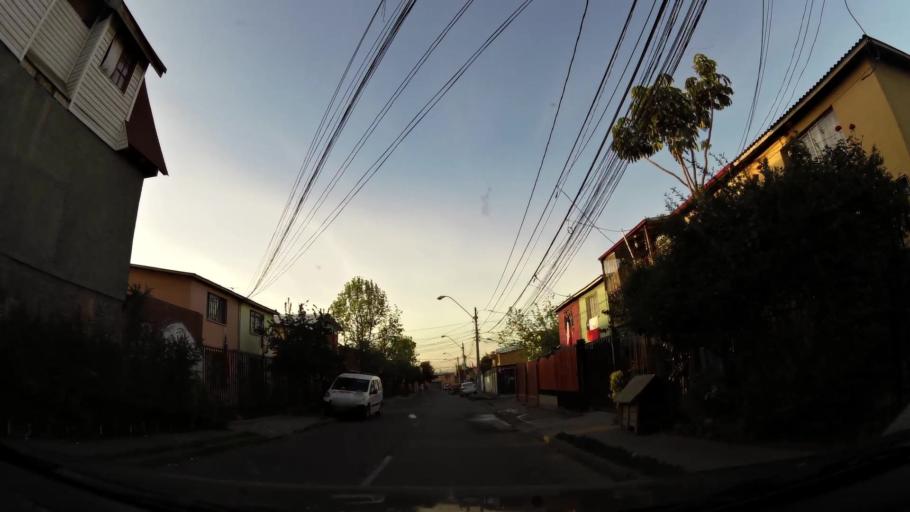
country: CL
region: Santiago Metropolitan
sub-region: Provincia de Cordillera
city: Puente Alto
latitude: -33.5966
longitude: -70.5616
